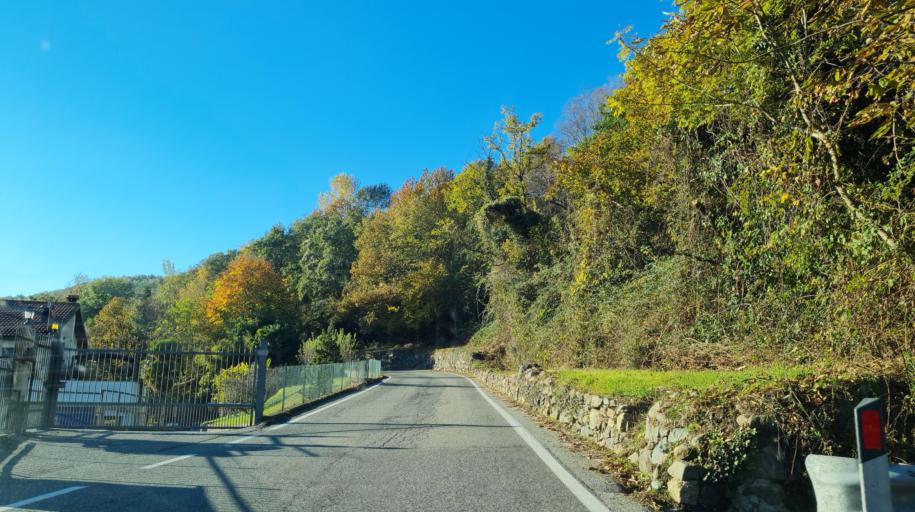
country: IT
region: Piedmont
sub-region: Provincia di Torino
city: Lessolo
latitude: 45.4737
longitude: 7.8072
